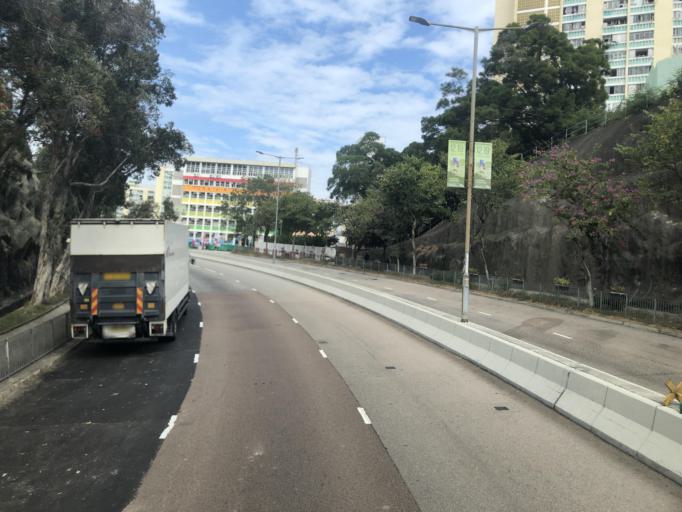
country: HK
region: Tsuen Wan
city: Tsuen Wan
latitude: 22.3469
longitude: 114.1079
